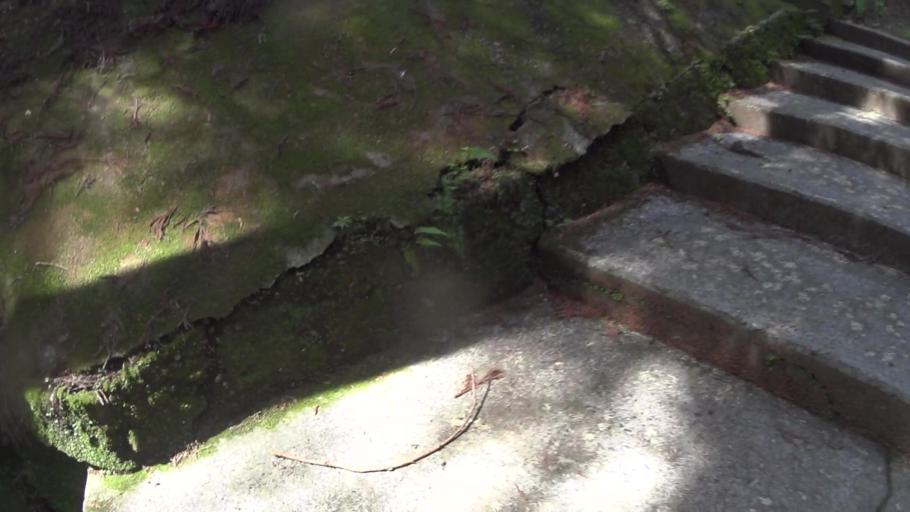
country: JP
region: Shiga Prefecture
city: Otsu-shi
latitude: 35.0966
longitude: 135.8523
